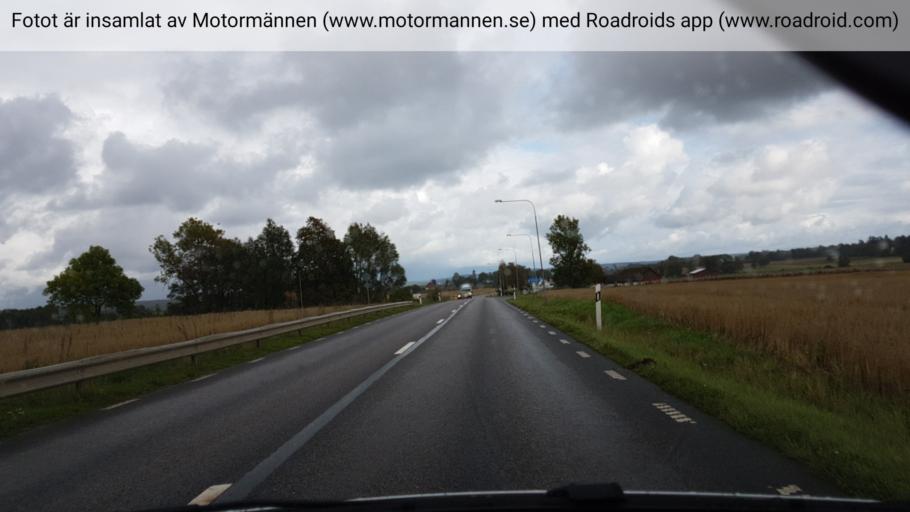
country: SE
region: Joenkoeping
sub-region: Mullsjo Kommun
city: Mullsjoe
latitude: 58.0813
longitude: 13.7769
